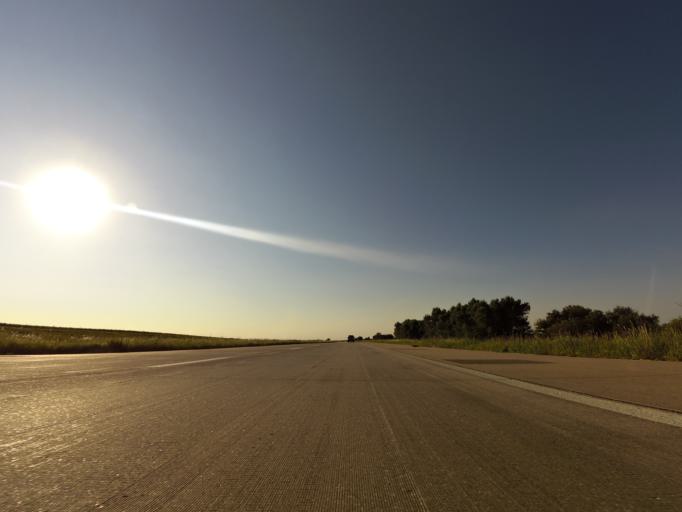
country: US
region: Kansas
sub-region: Sedgwick County
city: Colwich
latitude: 37.8330
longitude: -97.5645
